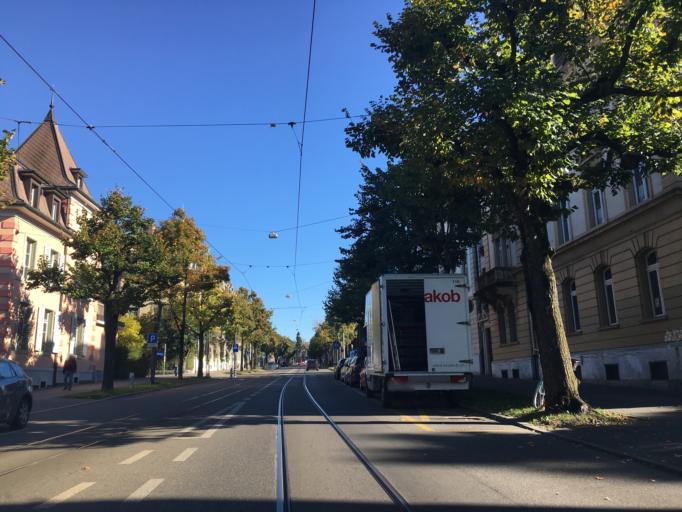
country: CH
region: Bern
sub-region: Bern-Mittelland District
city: Bern
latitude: 46.9423
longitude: 7.4535
